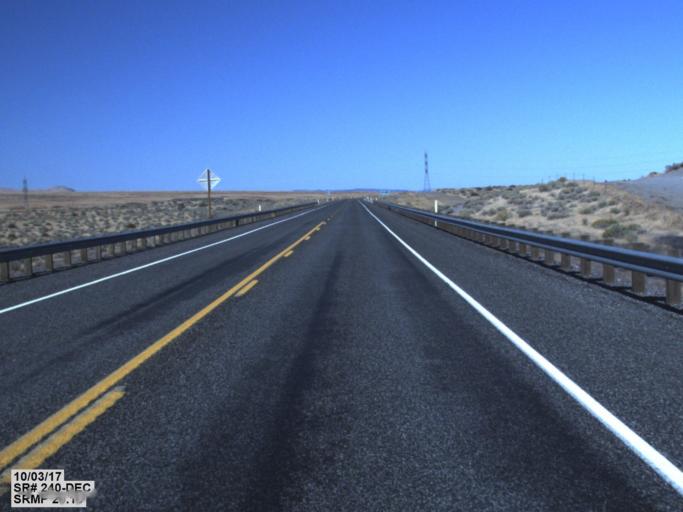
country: US
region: Washington
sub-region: Benton County
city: West Richland
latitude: 46.3865
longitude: -119.4286
